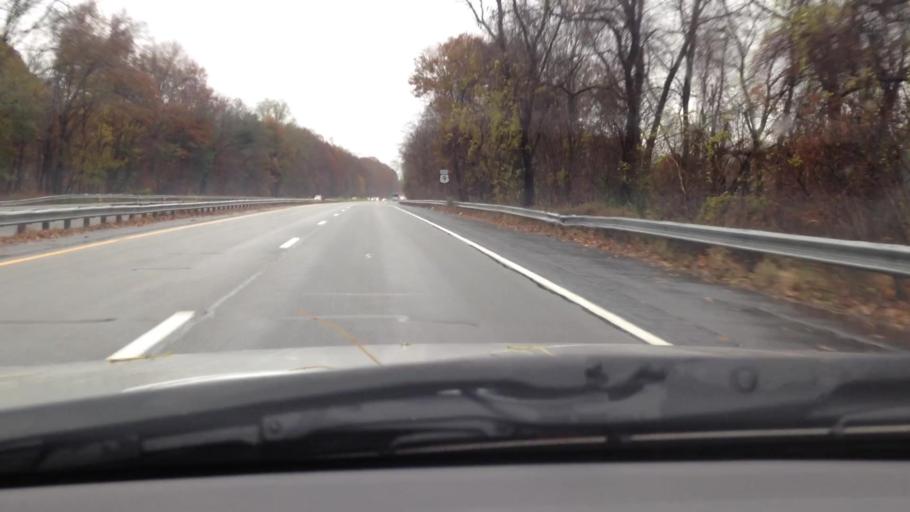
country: US
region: New York
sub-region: Westchester County
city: Buchanan
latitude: 41.2628
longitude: -73.9323
